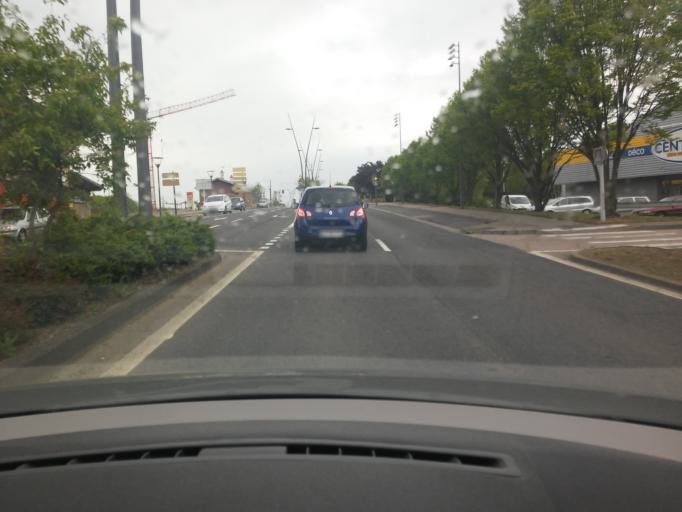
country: FR
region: Lorraine
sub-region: Departement de Meurthe-et-Moselle
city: Laxou
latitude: 48.6947
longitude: 6.1278
